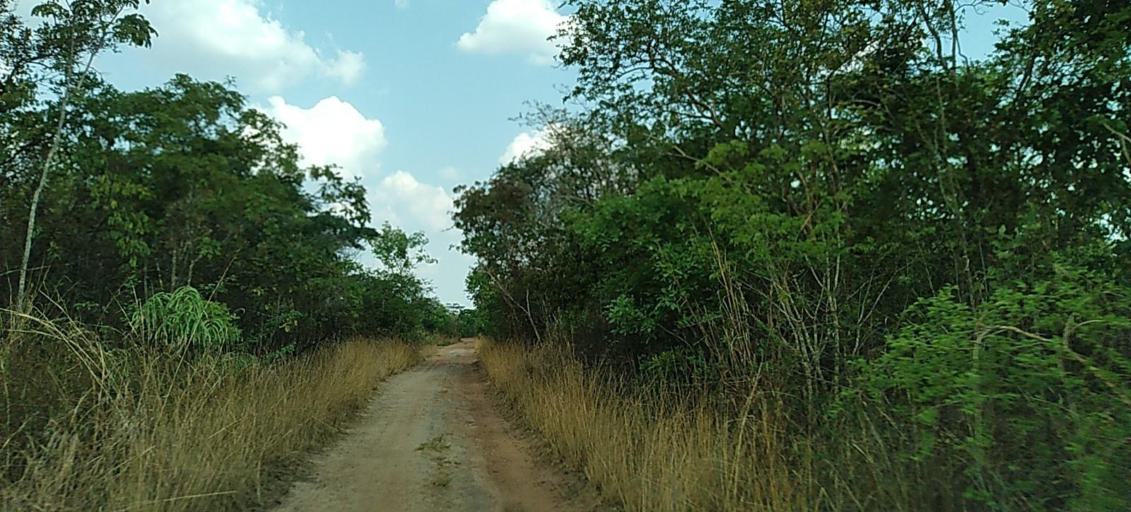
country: ZM
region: Copperbelt
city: Luanshya
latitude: -13.1549
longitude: 28.3224
